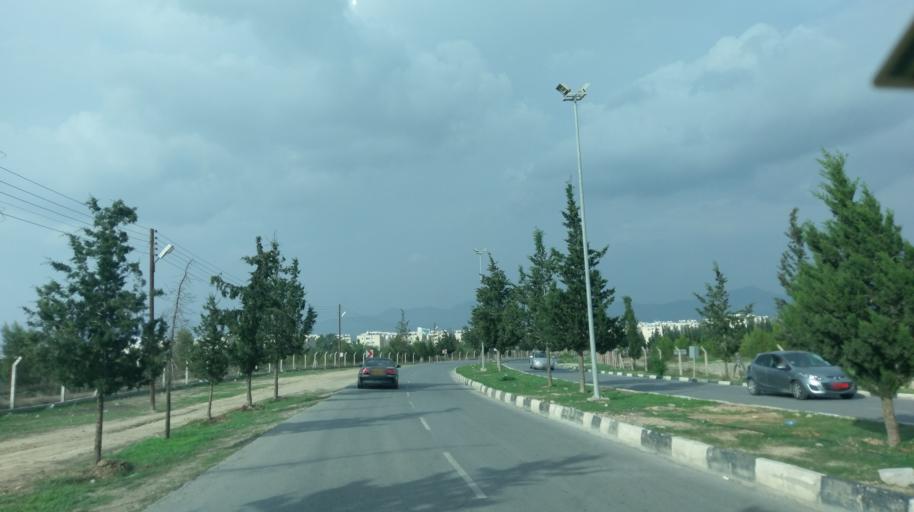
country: CY
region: Lefkosia
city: Nicosia
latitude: 35.1839
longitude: 33.3227
